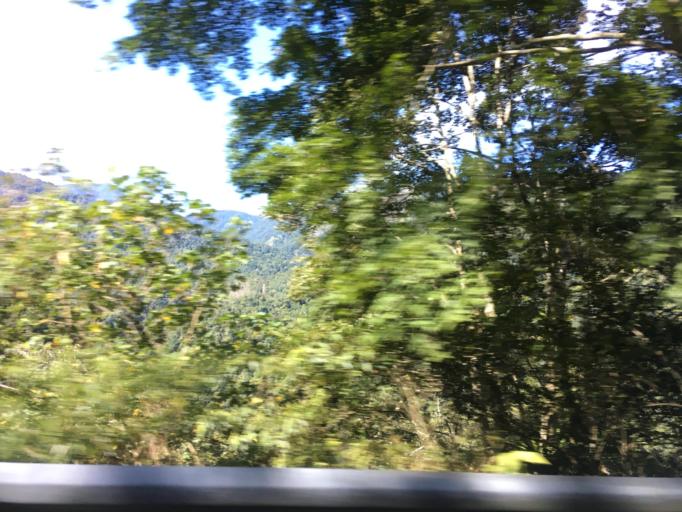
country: TW
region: Taiwan
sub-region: Yilan
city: Yilan
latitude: 24.5538
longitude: 121.5098
